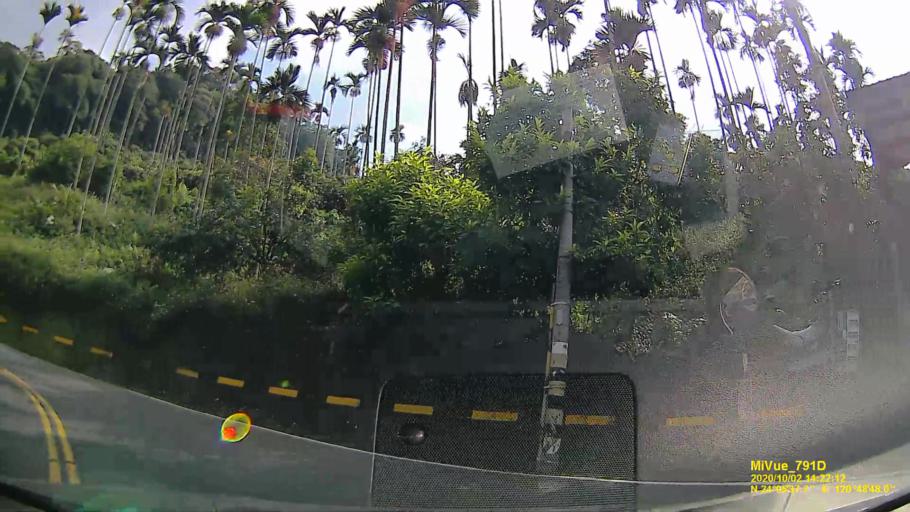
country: TW
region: Taiwan
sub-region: Taichung City
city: Taichung
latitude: 24.0938
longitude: 120.8133
